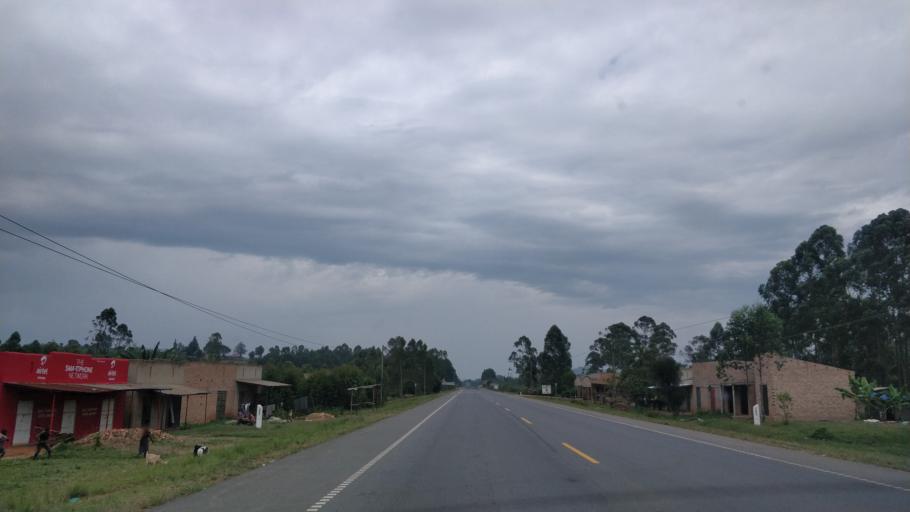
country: UG
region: Western Region
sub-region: Sheema District
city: Kibingo
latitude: -0.6723
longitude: 30.4297
